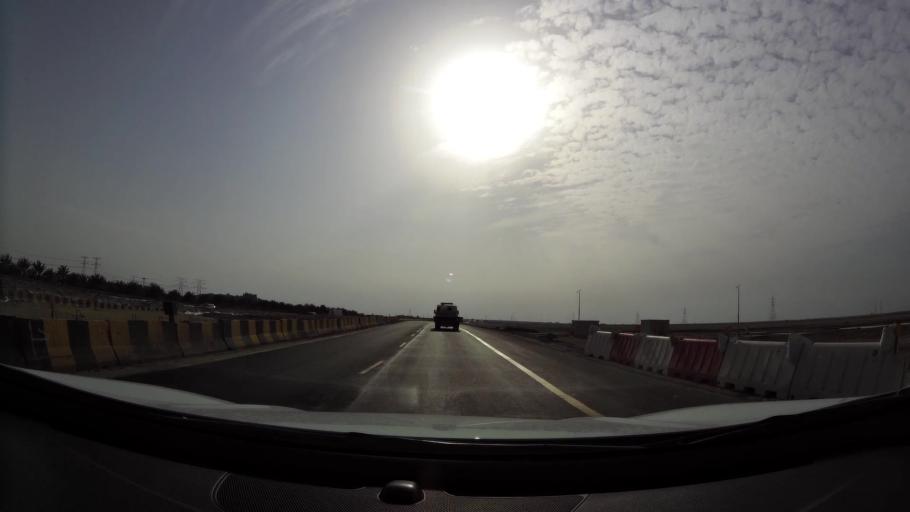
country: AE
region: Abu Dhabi
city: Abu Dhabi
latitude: 24.2198
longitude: 54.4287
